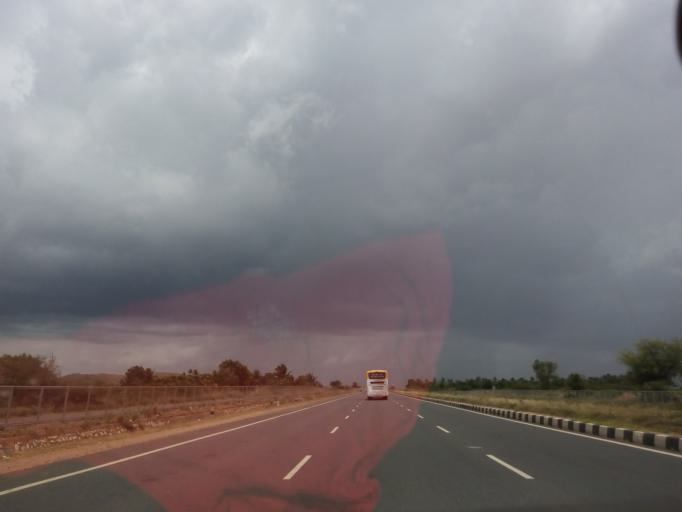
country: IN
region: Karnataka
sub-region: Chitradurga
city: Chitradurga
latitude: 14.1629
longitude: 76.4782
